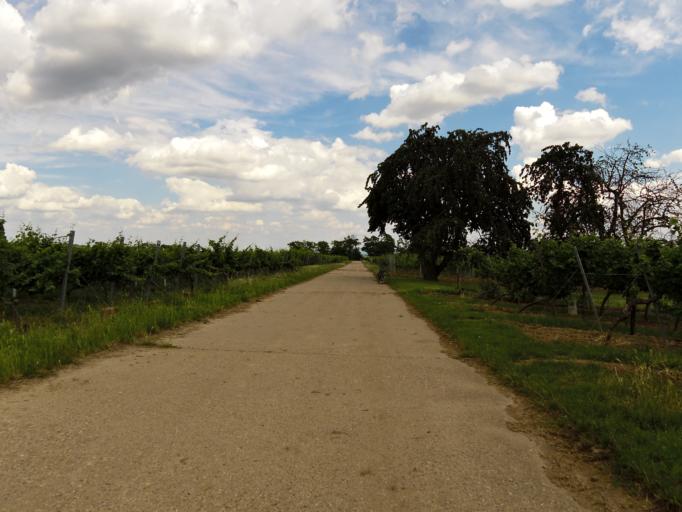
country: DE
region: Rheinland-Pfalz
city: Dackenheim
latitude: 49.5226
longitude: 8.1916
